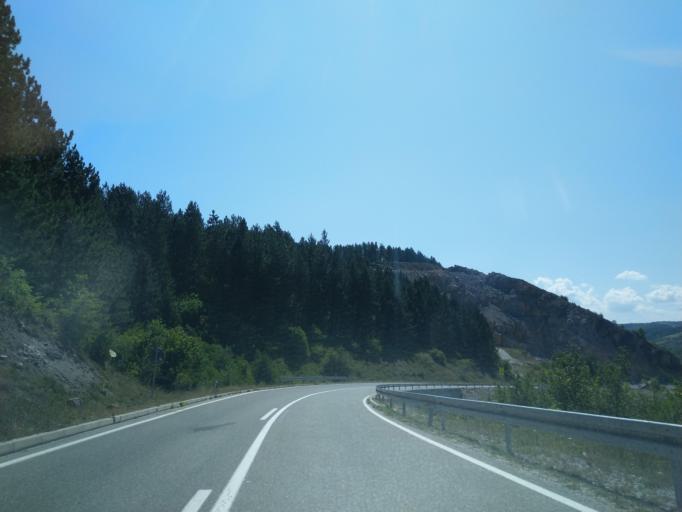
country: RS
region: Central Serbia
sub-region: Zlatiborski Okrug
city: Sjenica
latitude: 43.2997
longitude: 19.9356
